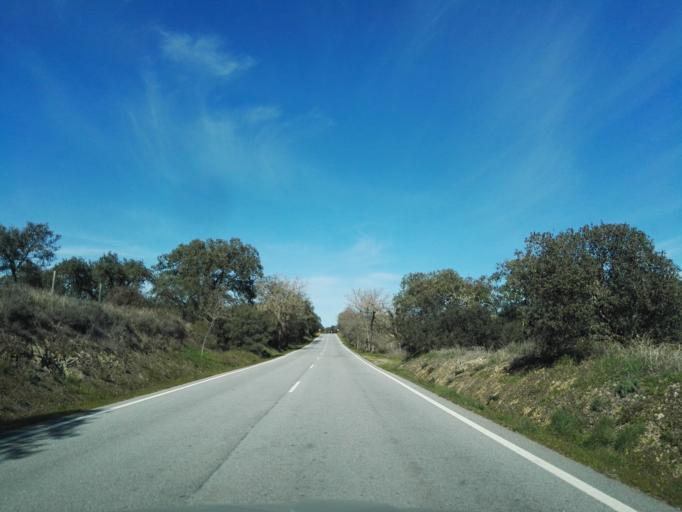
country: PT
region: Portalegre
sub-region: Arronches
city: Arronches
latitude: 39.0708
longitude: -7.2770
